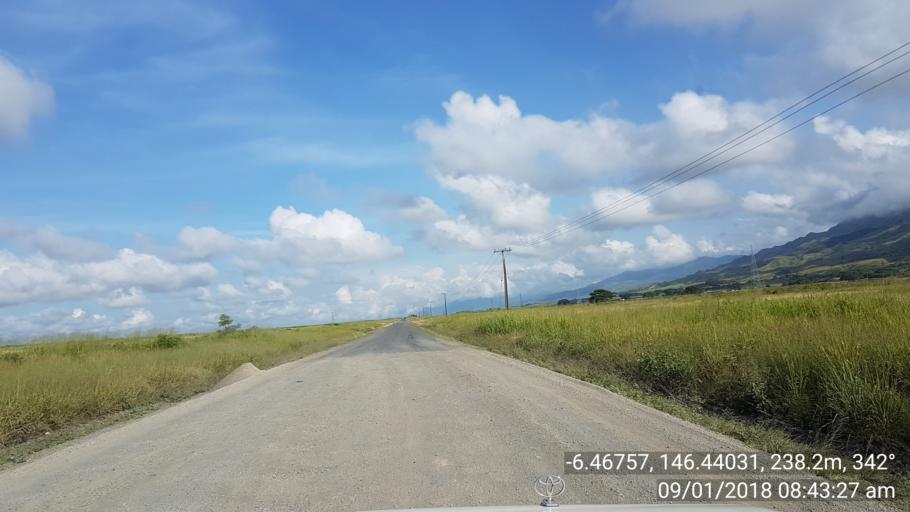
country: PG
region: Morobe
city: Lae
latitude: -6.4674
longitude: 146.4403
